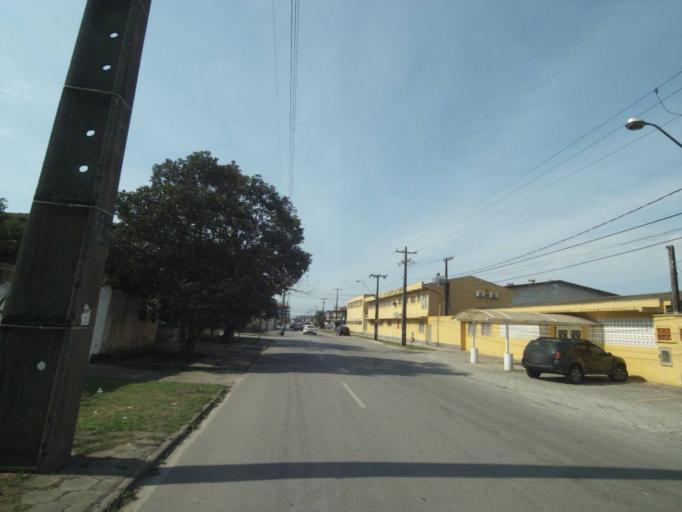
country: BR
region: Parana
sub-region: Paranagua
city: Paranagua
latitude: -25.5255
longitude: -48.5246
